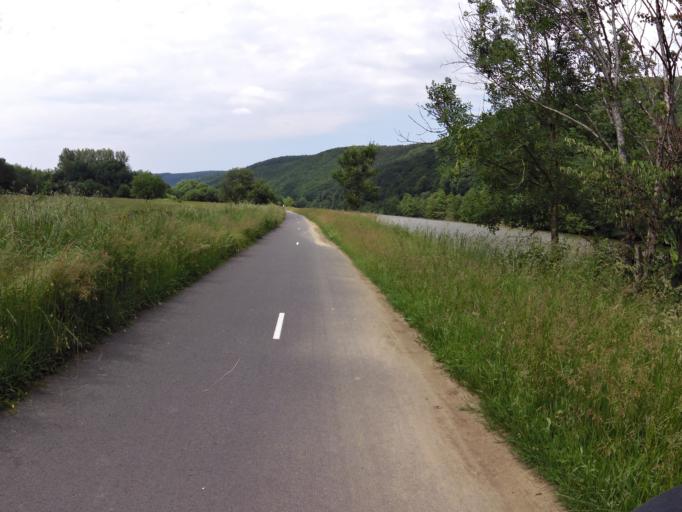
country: FR
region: Champagne-Ardenne
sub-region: Departement des Ardennes
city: Neufmanil
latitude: 49.8408
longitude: 4.7808
